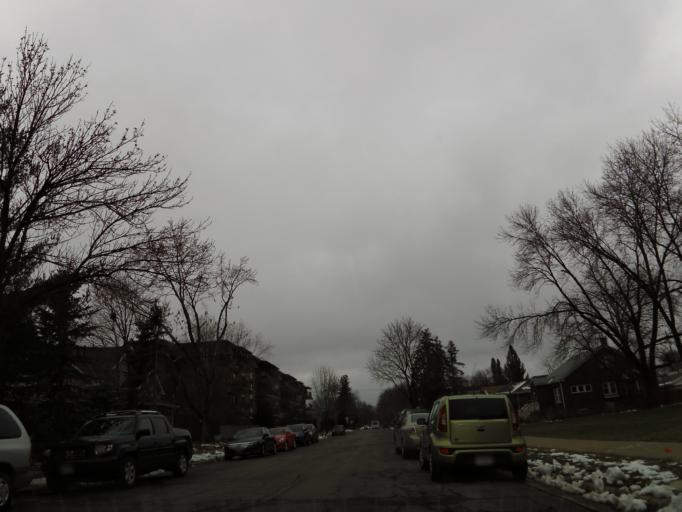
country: US
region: Minnesota
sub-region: Hennepin County
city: Minnetonka Mills
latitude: 44.9249
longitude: -93.4152
